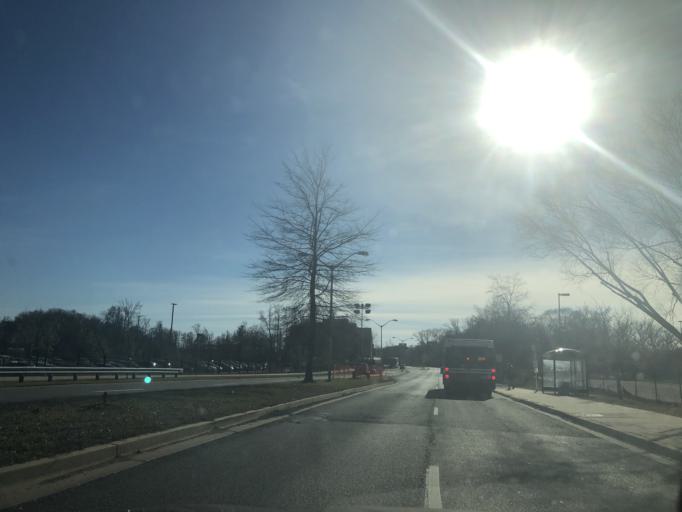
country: US
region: Maryland
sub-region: Prince George's County
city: College Park
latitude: 38.9764
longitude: -76.9276
